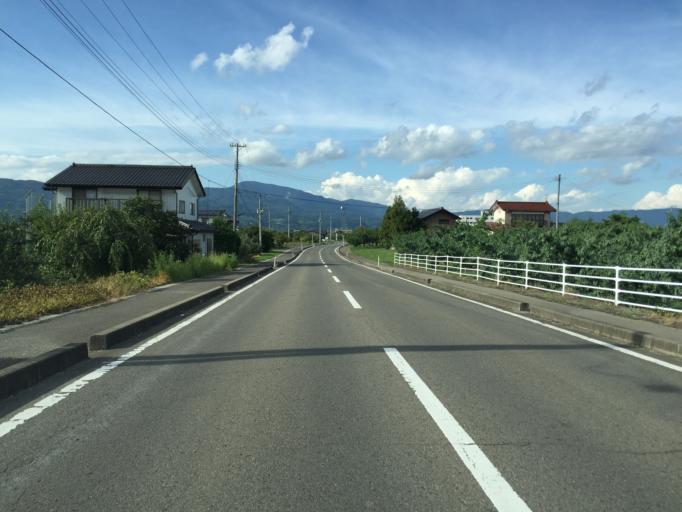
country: JP
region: Fukushima
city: Hobaramachi
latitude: 37.8128
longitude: 140.5211
